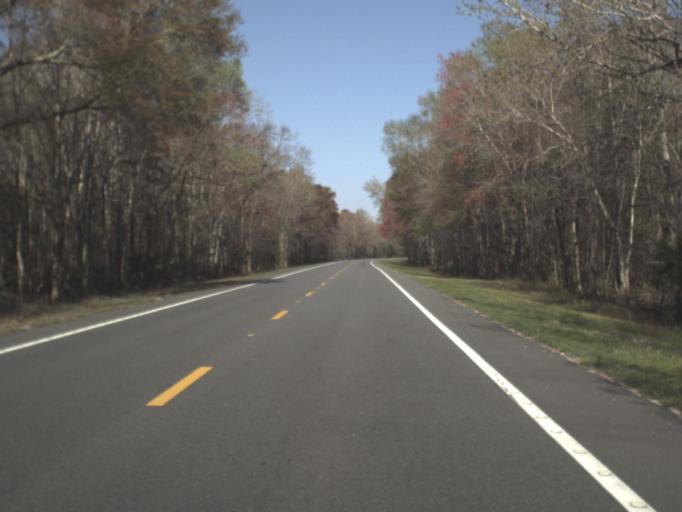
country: US
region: Florida
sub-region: Leon County
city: Woodville
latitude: 30.1563
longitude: -83.9947
